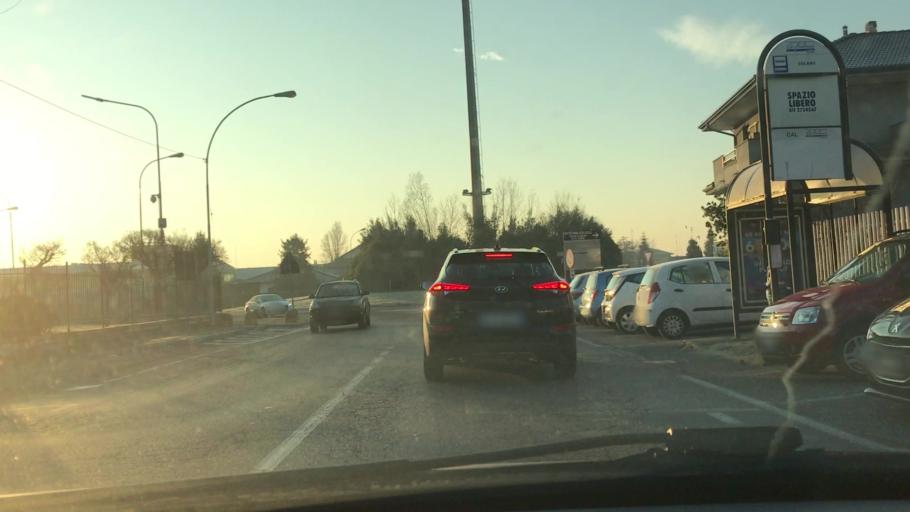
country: IT
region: Lombardy
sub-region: Citta metropolitana di Milano
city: Solaro
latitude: 45.6114
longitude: 9.0925
